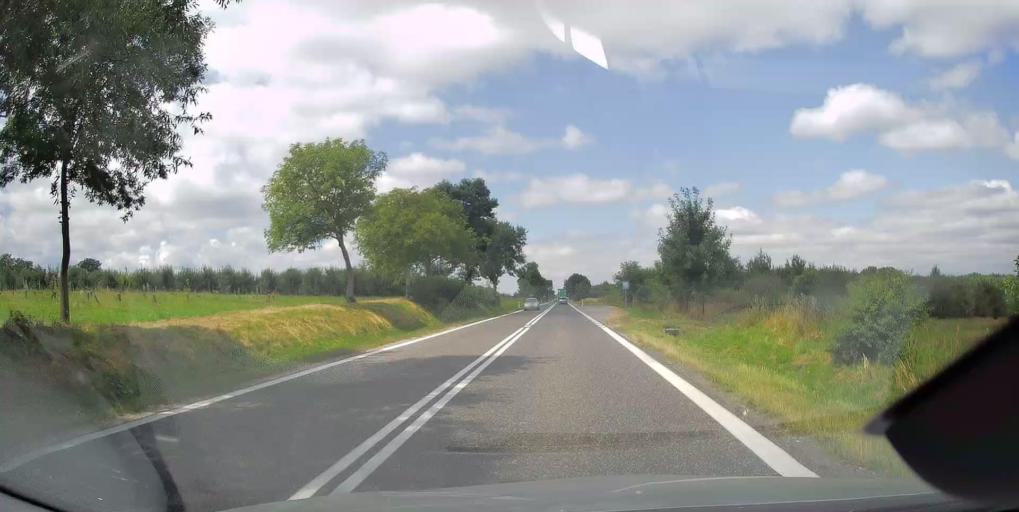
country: PL
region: Swietokrzyskie
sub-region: Powiat sandomierski
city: Loniow
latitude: 50.5819
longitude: 21.4933
